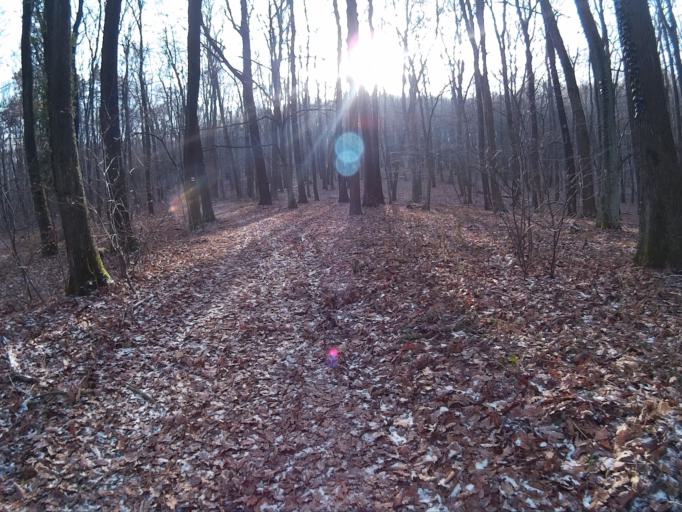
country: HU
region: Fejer
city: Szarliget
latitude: 47.4895
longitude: 18.4101
